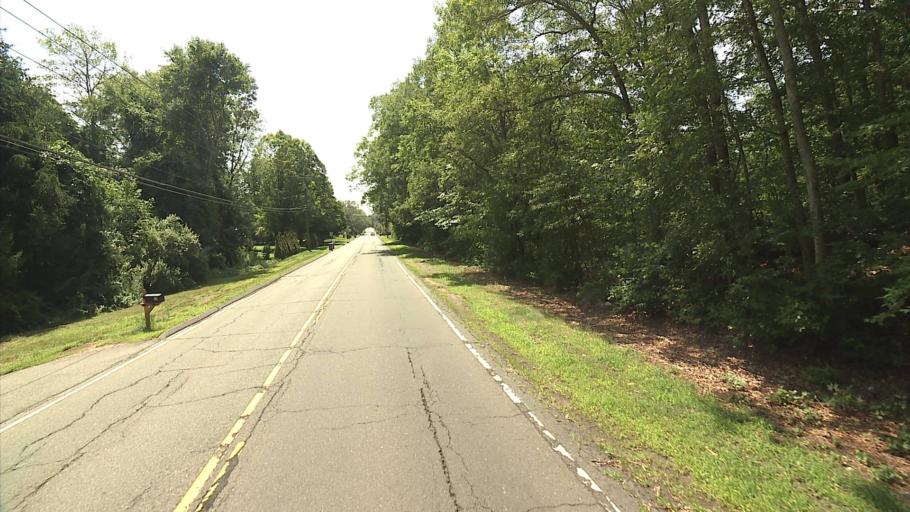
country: US
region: Connecticut
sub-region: Tolland County
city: Mansfield City
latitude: 41.7456
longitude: -72.2636
